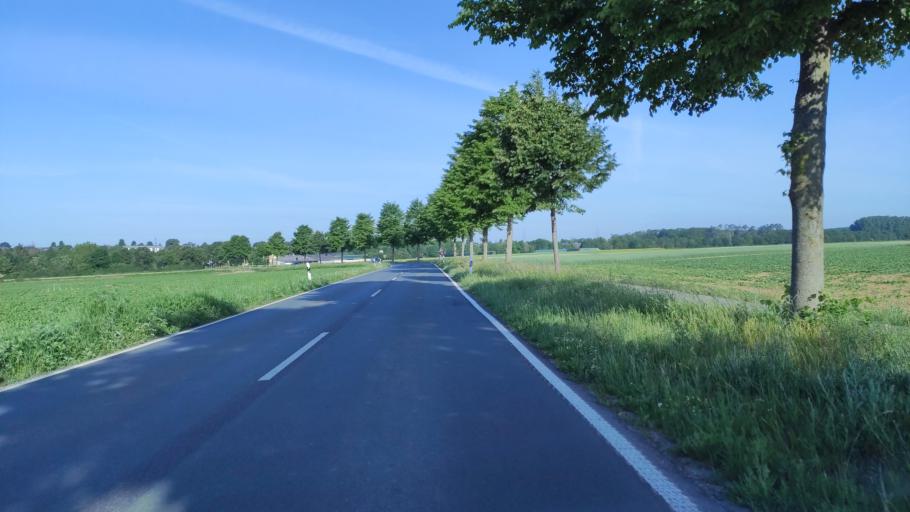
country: DE
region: North Rhine-Westphalia
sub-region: Regierungsbezirk Dusseldorf
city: Rommerskirchen
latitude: 51.1075
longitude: 6.7287
